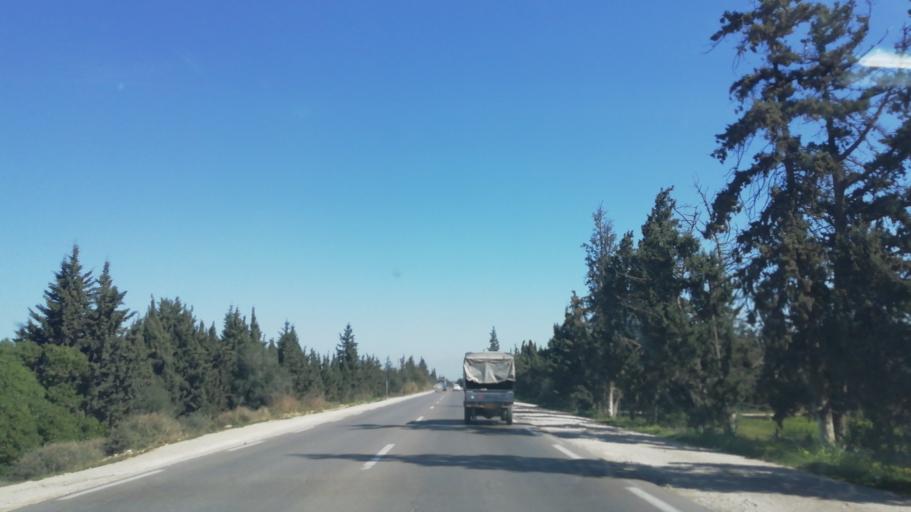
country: DZ
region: Mascara
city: Sig
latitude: 35.5556
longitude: -0.1043
